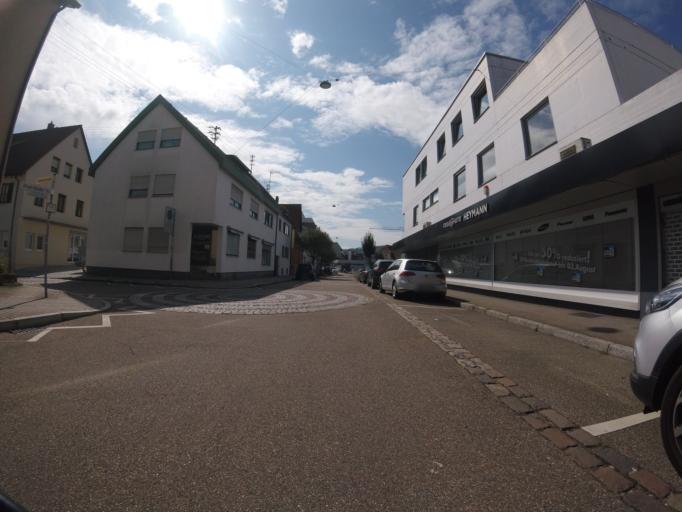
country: DE
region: Baden-Wuerttemberg
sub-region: Regierungsbezirk Stuttgart
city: Winnenden
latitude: 48.8786
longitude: 9.3954
